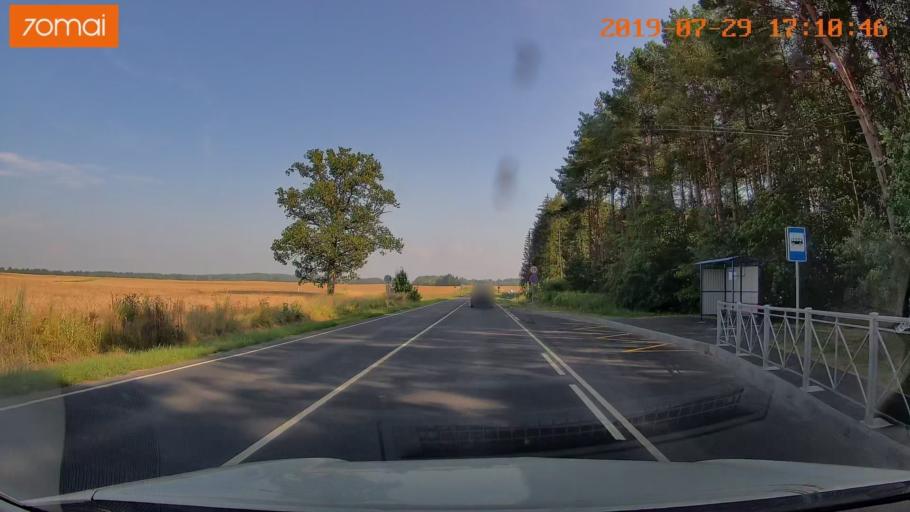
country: RU
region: Kaliningrad
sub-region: Gorod Kaliningrad
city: Kaliningrad
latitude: 54.7998
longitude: 20.3724
